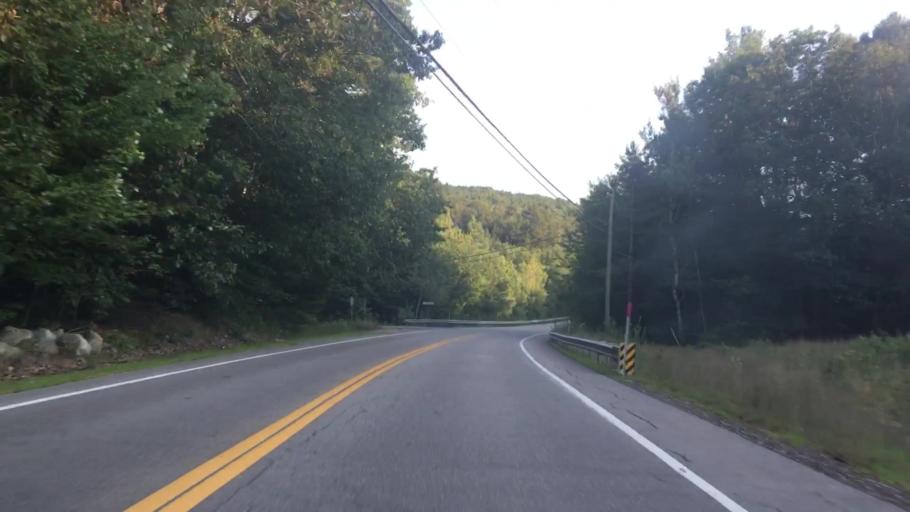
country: US
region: New Hampshire
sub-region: Belknap County
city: Gilmanton
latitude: 43.4466
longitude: -71.4195
